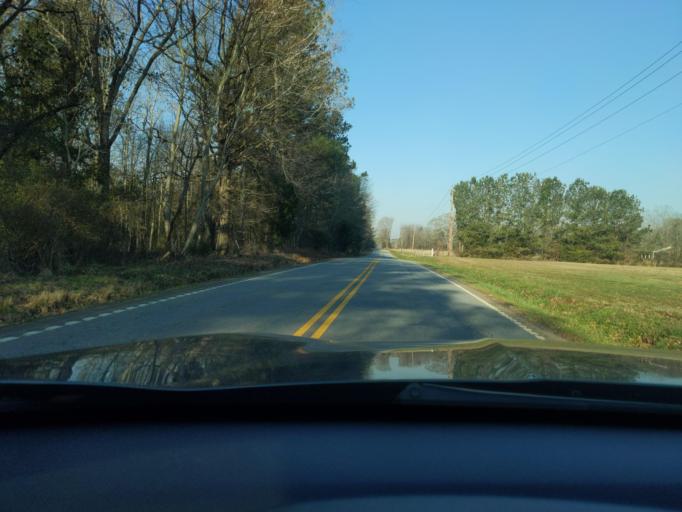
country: US
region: South Carolina
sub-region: Greenwood County
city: Ninety Six
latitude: 34.1723
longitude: -82.0832
